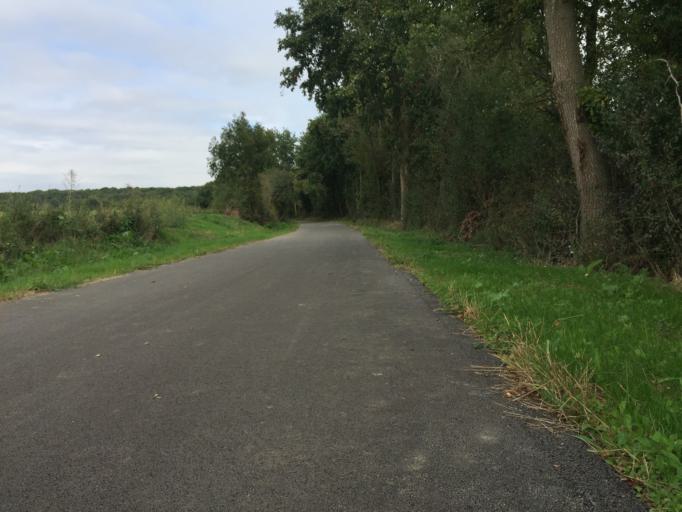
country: FR
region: Picardie
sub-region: Departement de l'Oise
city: Auneuil
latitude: 49.3940
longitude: 2.0125
